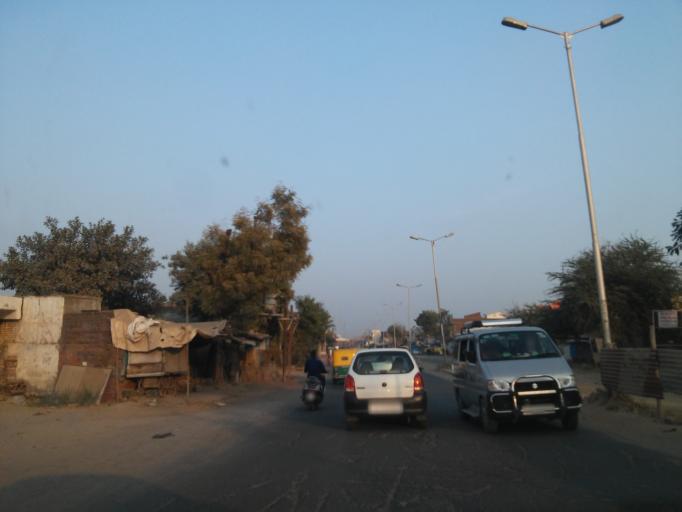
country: IN
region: Gujarat
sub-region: Ahmadabad
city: Sarkhej
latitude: 22.9871
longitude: 72.4979
